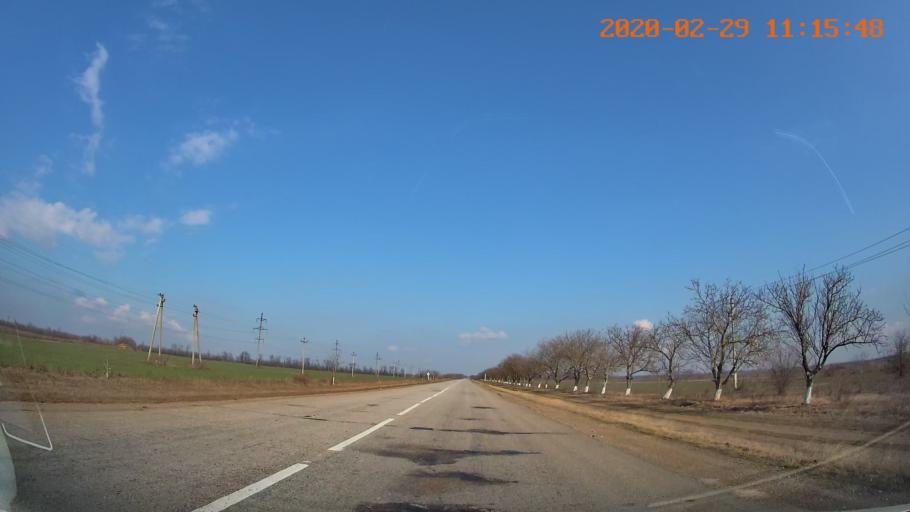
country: MD
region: Telenesti
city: Dubasari
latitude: 47.2996
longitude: 29.1661
